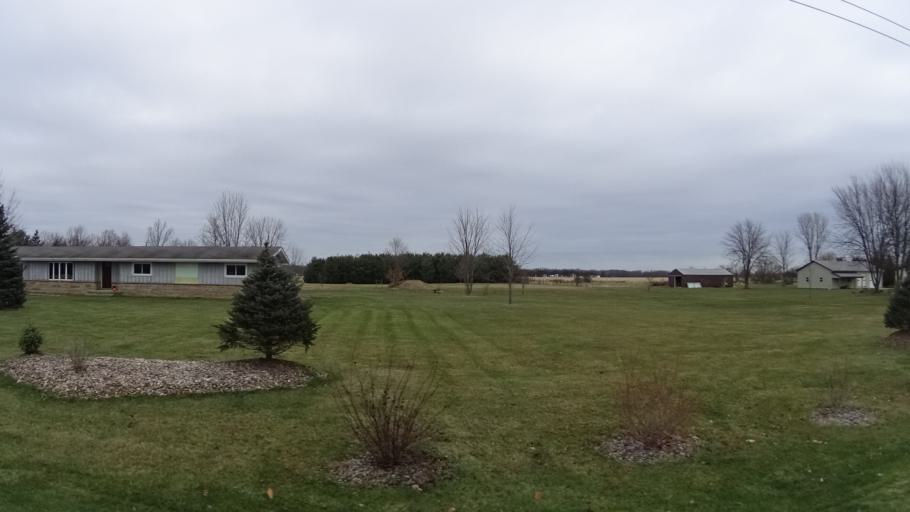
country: US
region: Ohio
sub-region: Lorain County
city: Wellington
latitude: 41.1895
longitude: -82.2146
